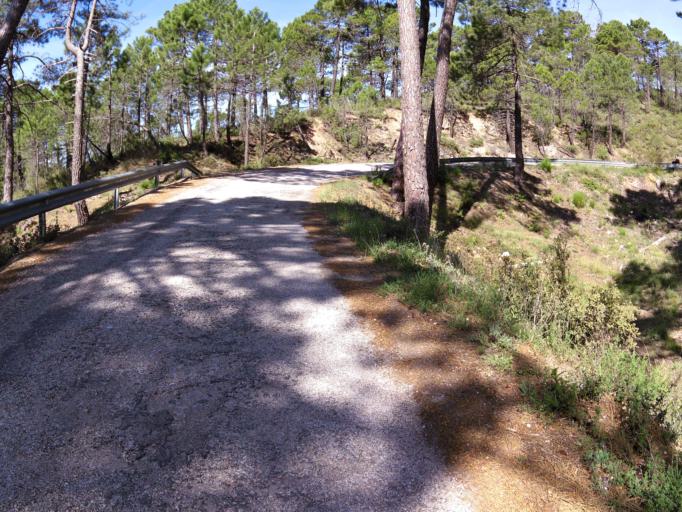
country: ES
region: Castille-La Mancha
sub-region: Provincia de Albacete
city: Riopar
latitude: 38.5236
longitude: -2.4371
